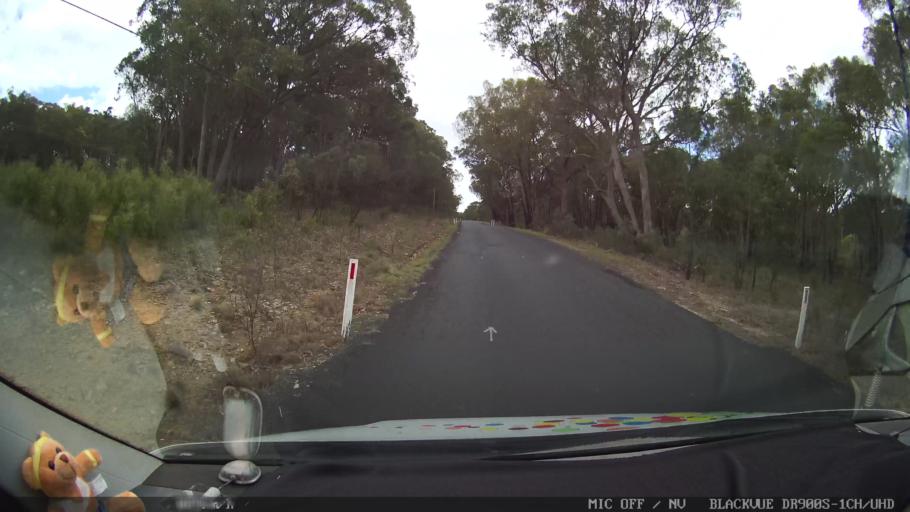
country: AU
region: New South Wales
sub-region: Glen Innes Severn
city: Glen Innes
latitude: -29.4362
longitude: 151.6304
